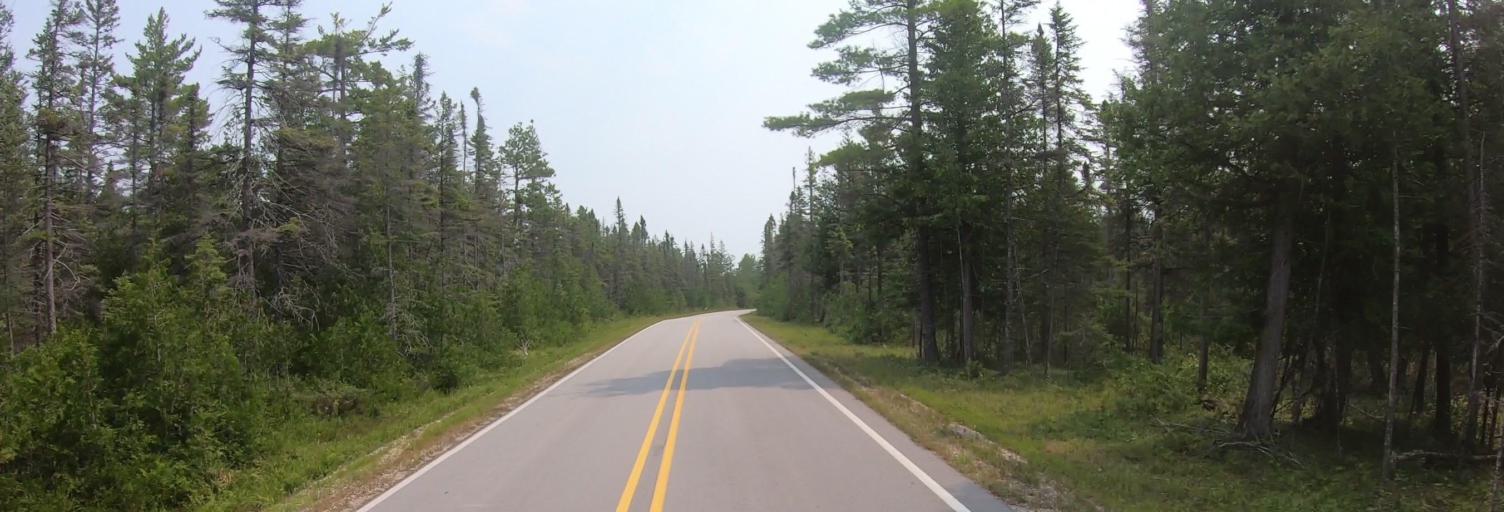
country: CA
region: Ontario
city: Thessalon
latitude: 45.9498
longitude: -83.6047
